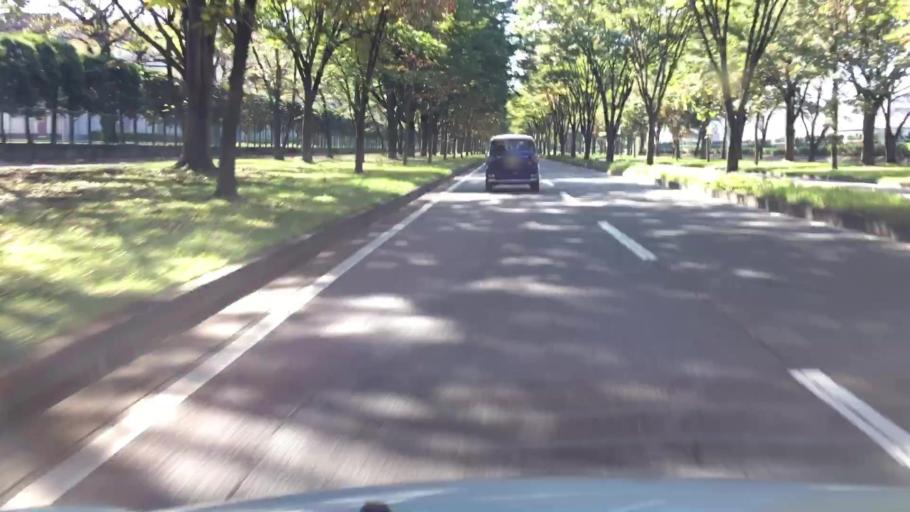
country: JP
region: Tochigi
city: Utsunomiya-shi
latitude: 36.5417
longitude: 139.9867
